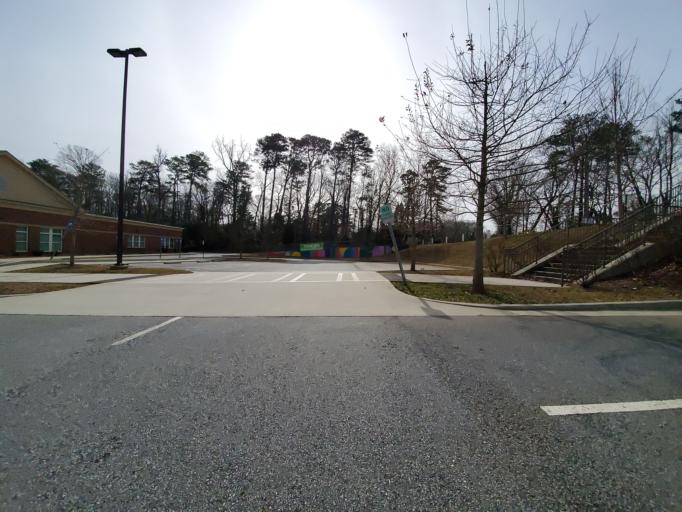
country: US
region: Georgia
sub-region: DeKalb County
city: North Decatur
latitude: 33.7783
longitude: -84.3169
